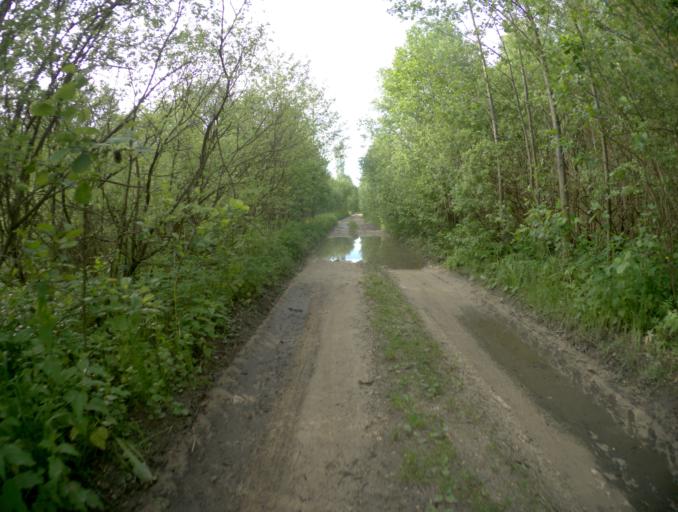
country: RU
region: Vladimir
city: Zolotkovo
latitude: 55.4126
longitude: 40.9084
